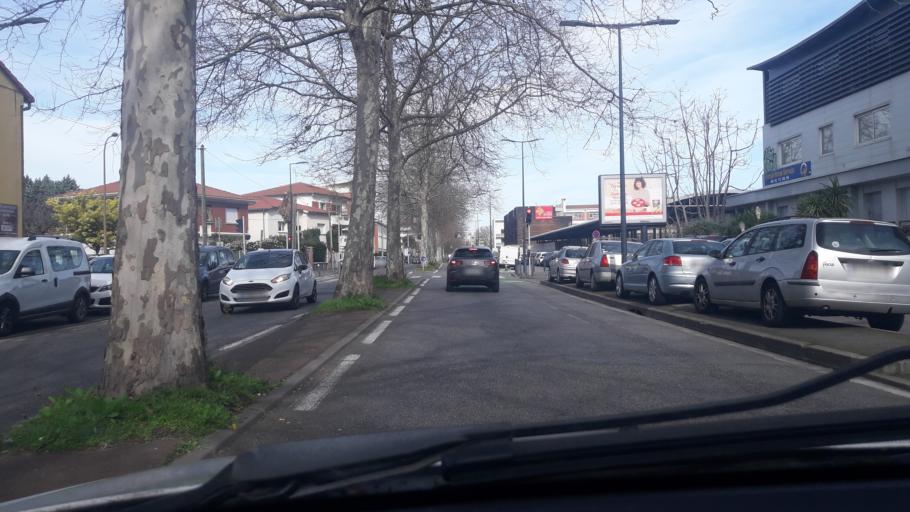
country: FR
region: Midi-Pyrenees
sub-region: Departement de la Haute-Garonne
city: Toulouse
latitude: 43.5716
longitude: 1.4244
